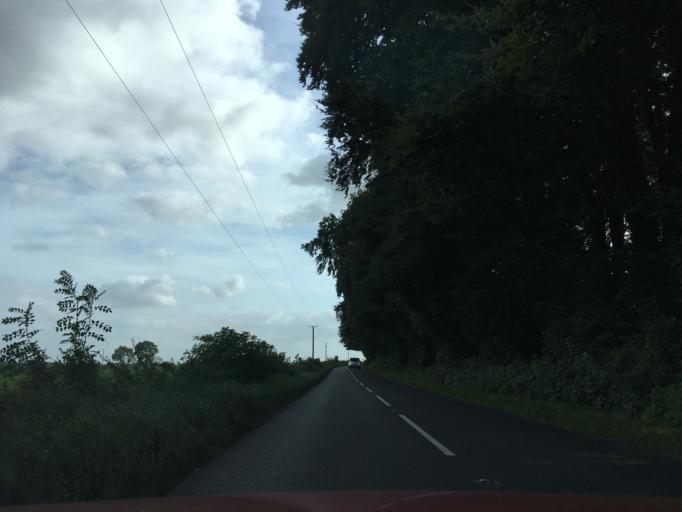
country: GB
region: England
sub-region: Gloucestershire
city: Nailsworth
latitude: 51.6808
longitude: -2.2761
